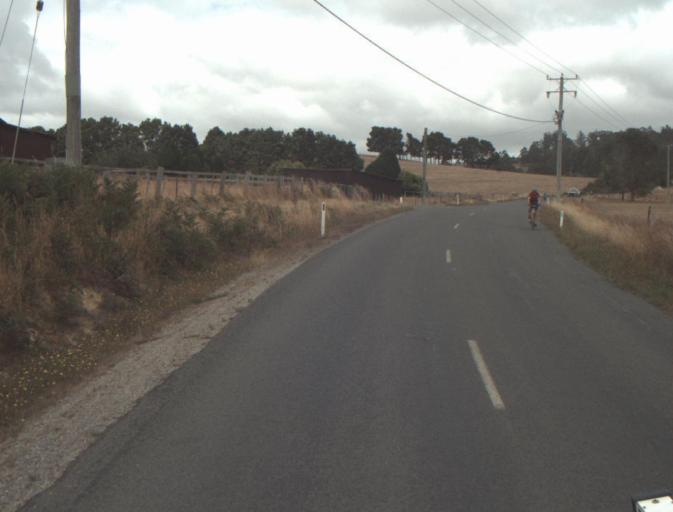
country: AU
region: Tasmania
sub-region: Launceston
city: Mayfield
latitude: -41.1938
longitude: 147.2209
